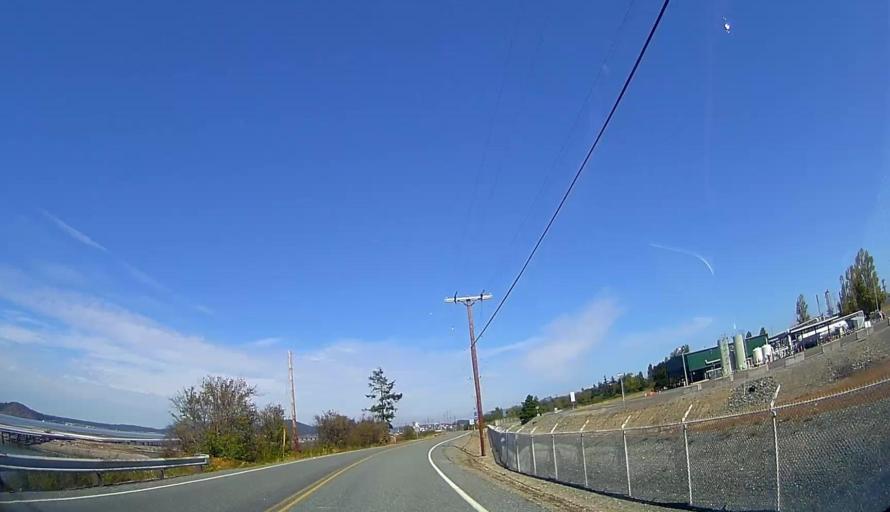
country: US
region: Washington
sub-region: Skagit County
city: Anacortes
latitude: 48.4913
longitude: -122.5751
